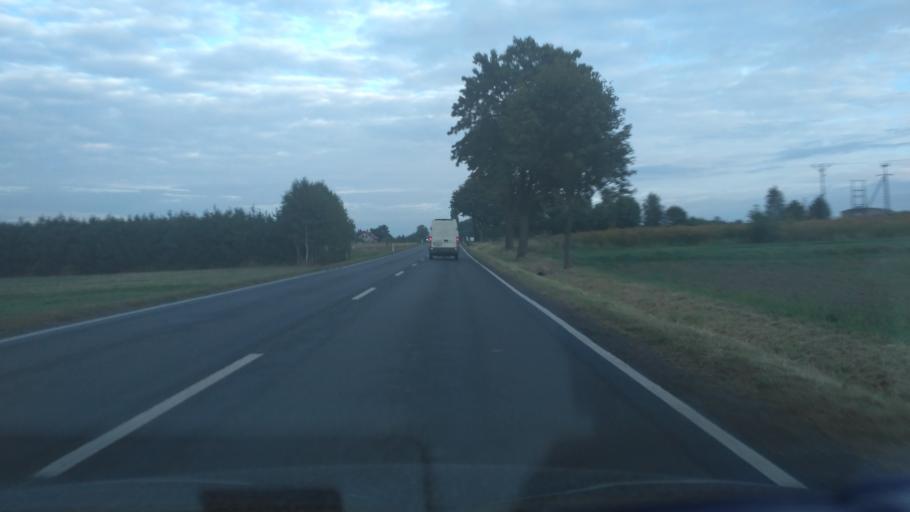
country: PL
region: Lublin Voivodeship
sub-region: Powiat leczynski
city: Spiczyn
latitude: 51.3034
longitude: 22.7388
